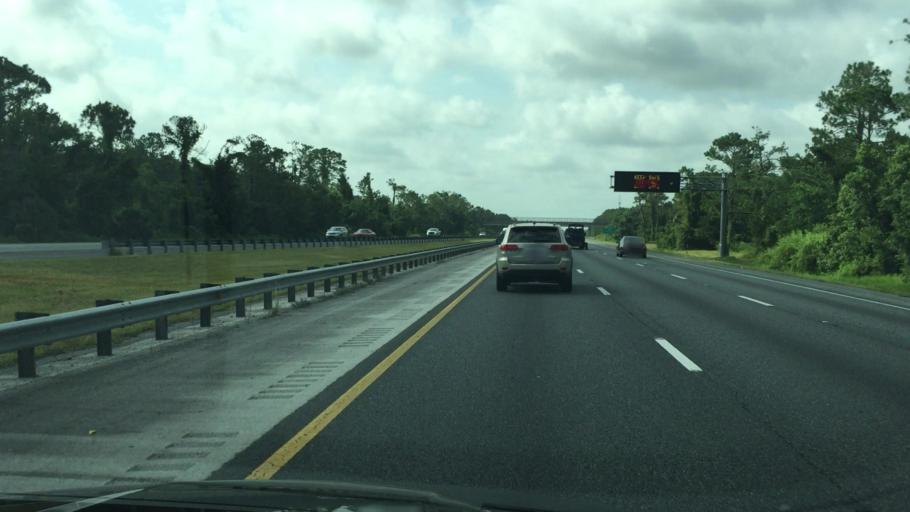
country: US
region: Florida
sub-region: Volusia County
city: Ormond Beach
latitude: 29.2778
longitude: -81.1235
